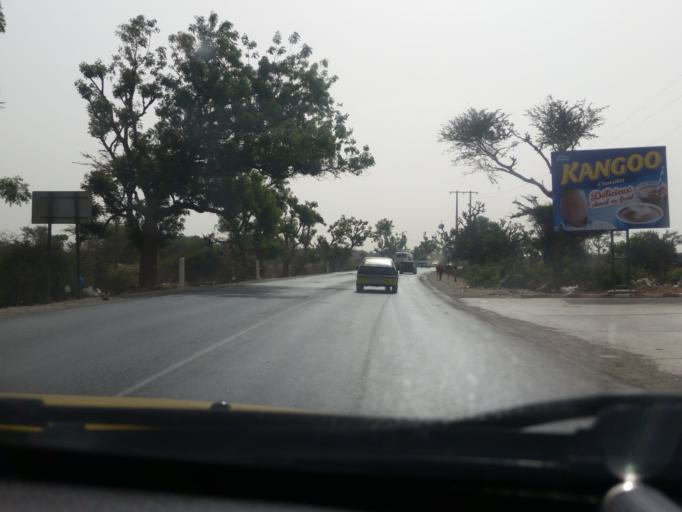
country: SN
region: Thies
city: Pout
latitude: 14.7656
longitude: -17.1066
